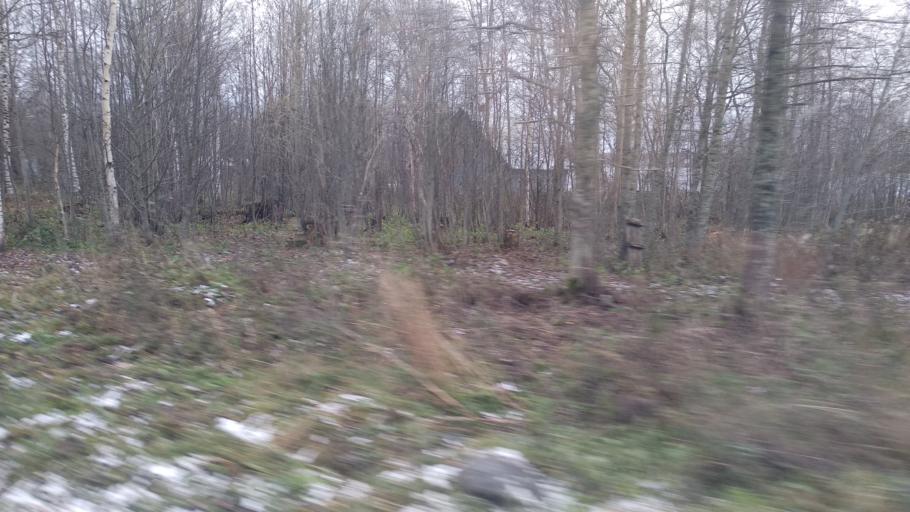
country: RU
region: Republic of Karelia
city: Shun'ga
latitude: 62.0852
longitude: 35.2052
